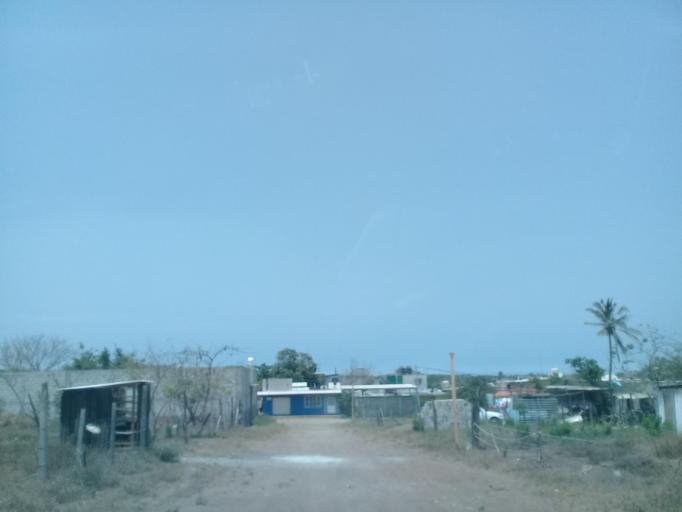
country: MX
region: Veracruz
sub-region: Veracruz
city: Las Amapolas
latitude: 19.1586
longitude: -96.2148
